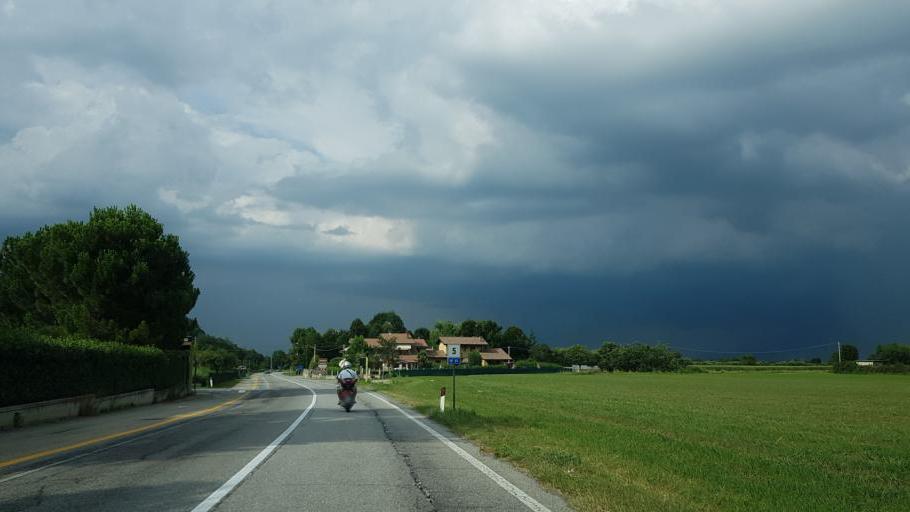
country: IT
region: Piedmont
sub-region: Provincia di Cuneo
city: Vignolo
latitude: 44.3683
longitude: 7.4742
